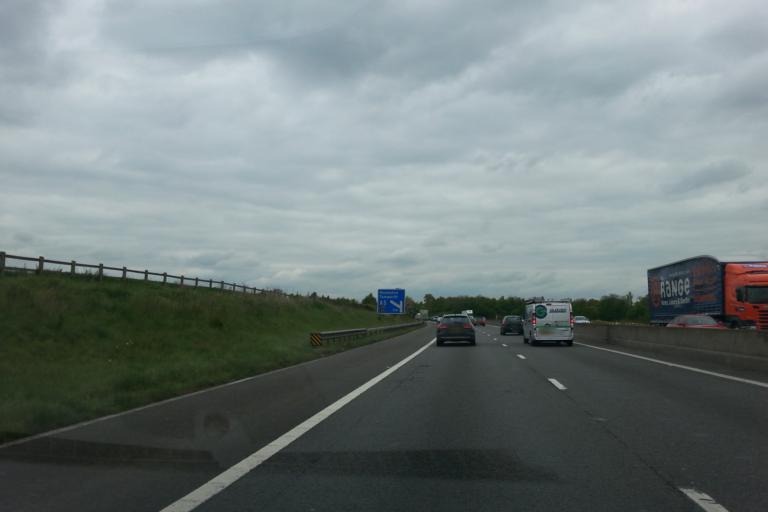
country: GB
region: England
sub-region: Warwickshire
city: Kingsbury
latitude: 52.5854
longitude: -1.6611
